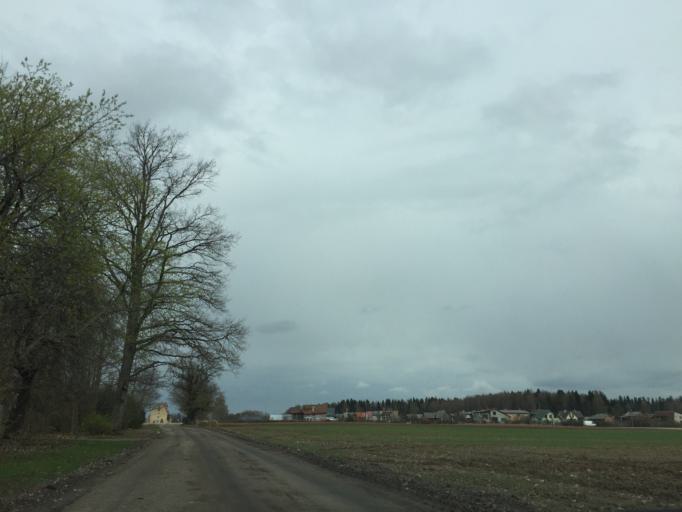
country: LV
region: Priekuli
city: Priekuli
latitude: 57.3079
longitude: 25.3396
